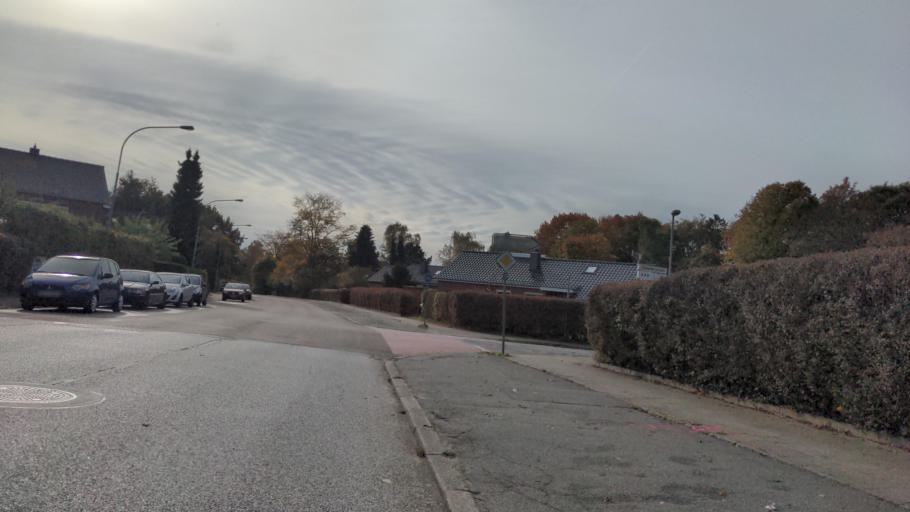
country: DE
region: Mecklenburg-Vorpommern
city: Selmsdorf
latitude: 53.9193
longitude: 10.8224
